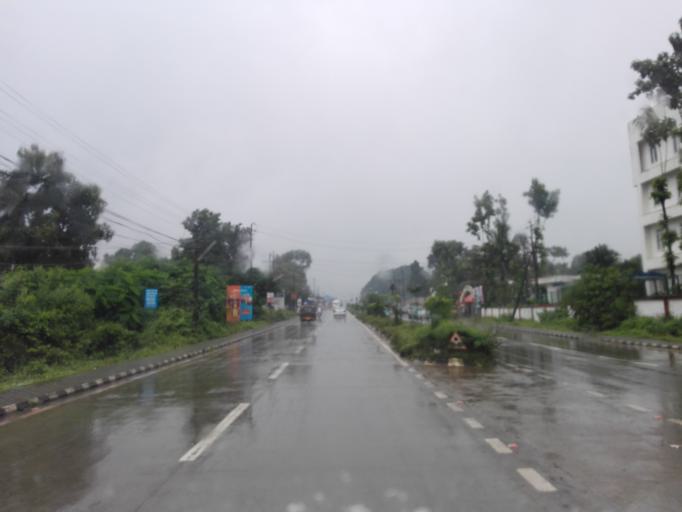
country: IN
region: Kerala
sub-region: Ernakulam
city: Elur
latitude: 10.0538
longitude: 76.3298
